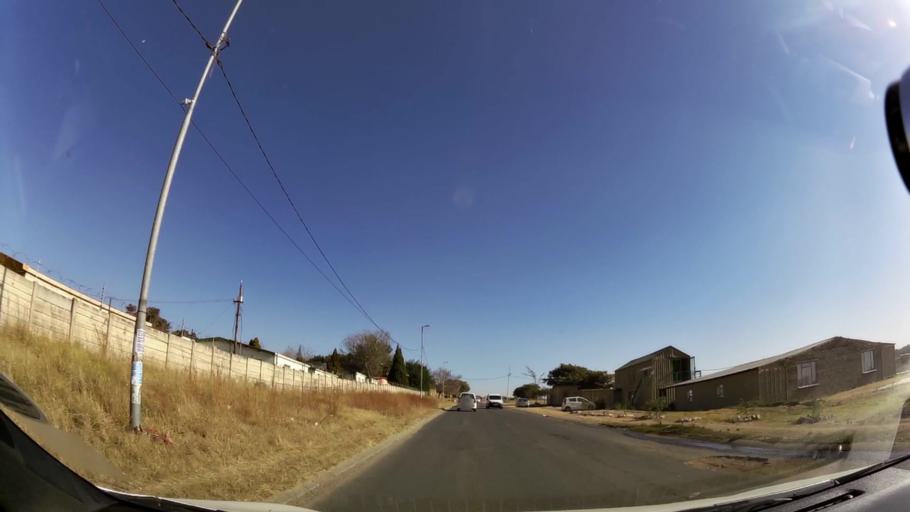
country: ZA
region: Gauteng
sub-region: City of Johannesburg Metropolitan Municipality
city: Diepsloot
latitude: -26.0223
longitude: 27.9658
